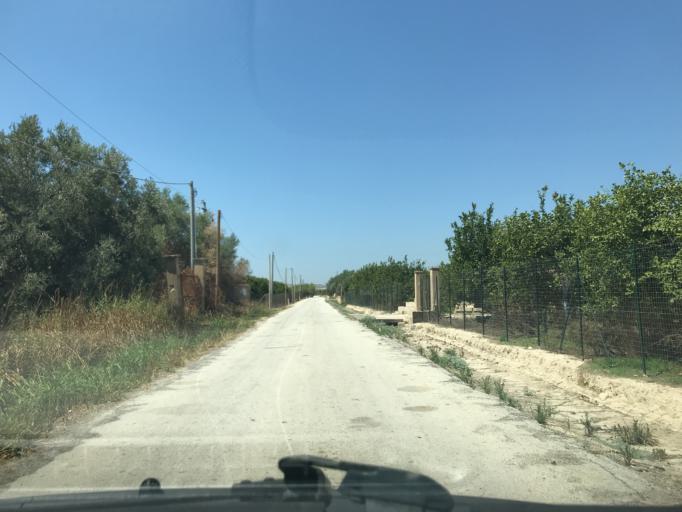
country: IT
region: Sicily
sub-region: Provincia di Siracusa
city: Noto
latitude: 36.8336
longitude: 15.0453
